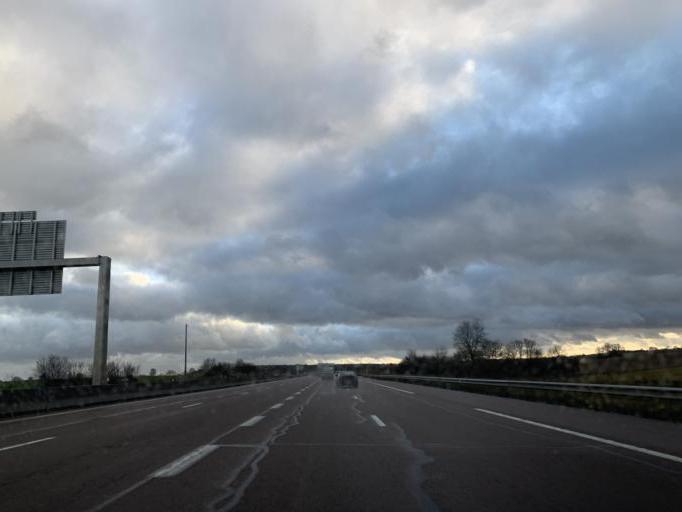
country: FR
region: Champagne-Ardenne
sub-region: Departement de la Haute-Marne
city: Rolampont
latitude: 47.9042
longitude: 5.2231
